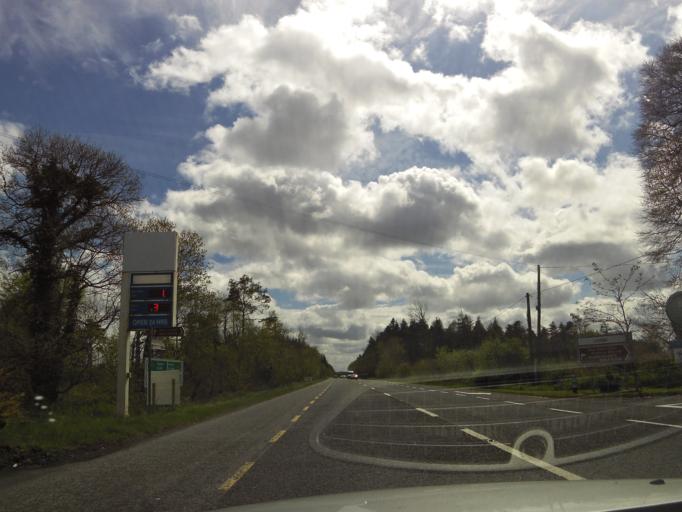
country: IE
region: Connaught
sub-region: Maigh Eo
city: Claremorris
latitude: 53.7023
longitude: -8.9802
